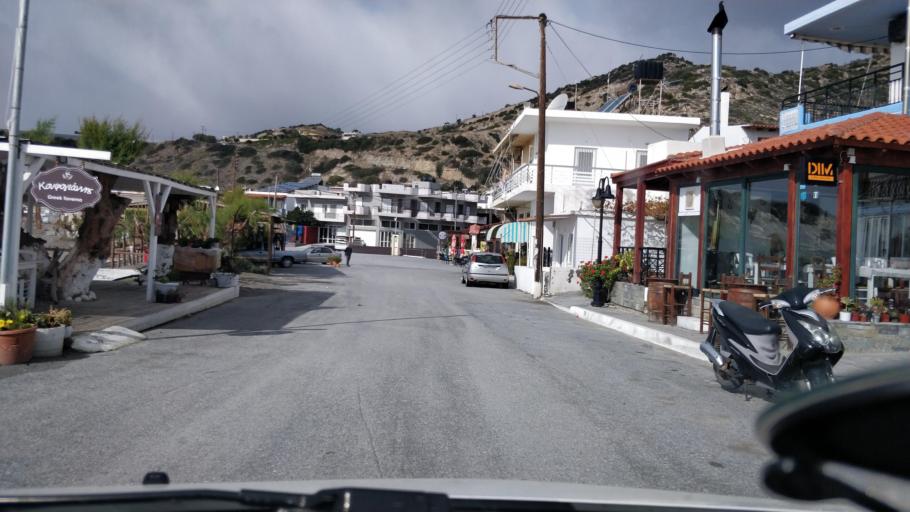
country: GR
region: Crete
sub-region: Nomos Lasithiou
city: Gra Liyia
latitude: 34.9845
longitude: 25.4985
